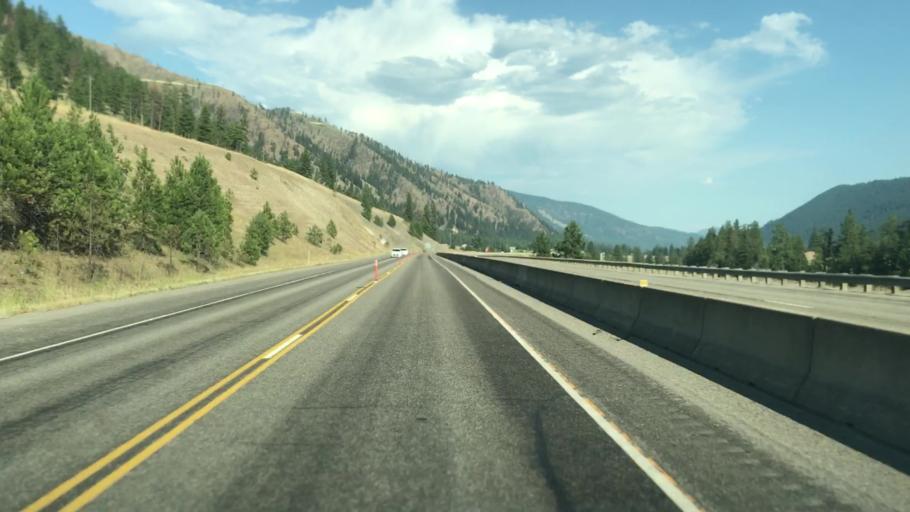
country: US
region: Montana
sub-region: Mineral County
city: Superior
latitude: 47.2172
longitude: -114.9535
